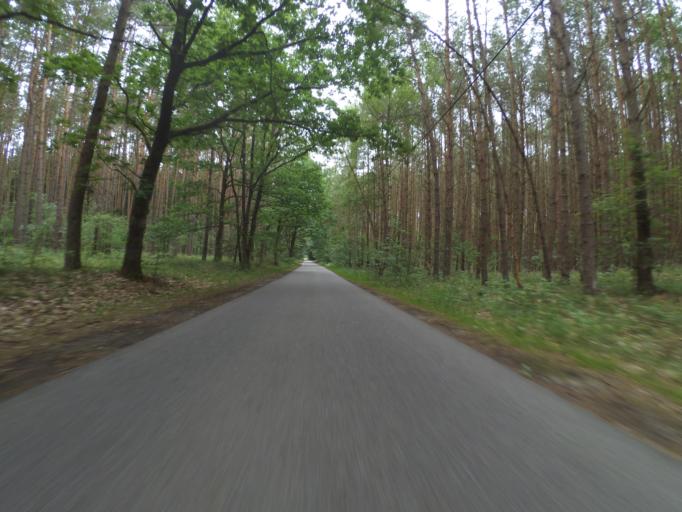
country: DE
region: Mecklenburg-Vorpommern
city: Dabel
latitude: 53.6487
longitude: 11.9545
